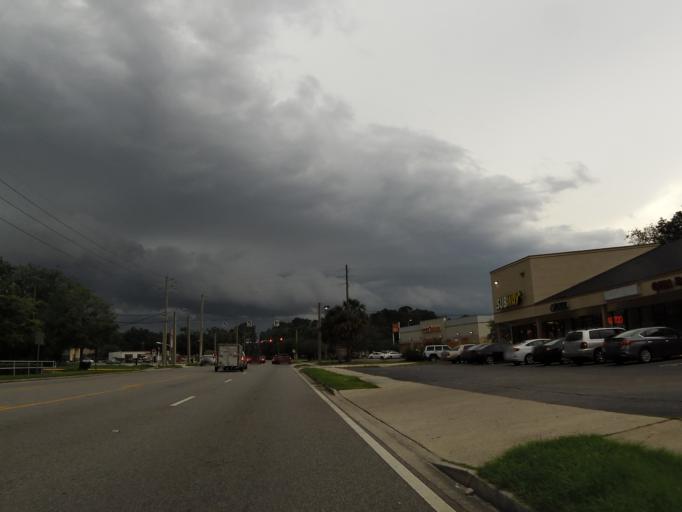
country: US
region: Florida
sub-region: Duval County
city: Jacksonville
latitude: 30.2871
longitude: -81.5786
